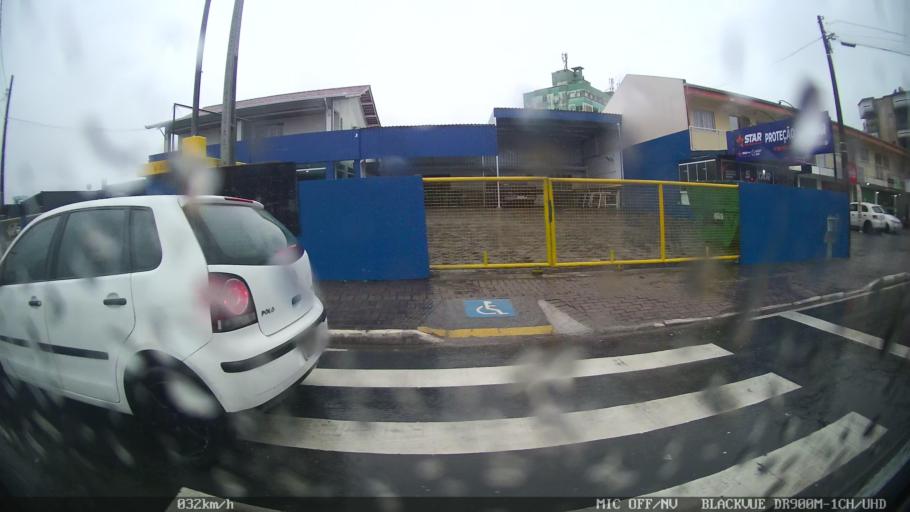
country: BR
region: Santa Catarina
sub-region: Balneario Camboriu
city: Balneario Camboriu
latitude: -27.0048
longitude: -48.6350
